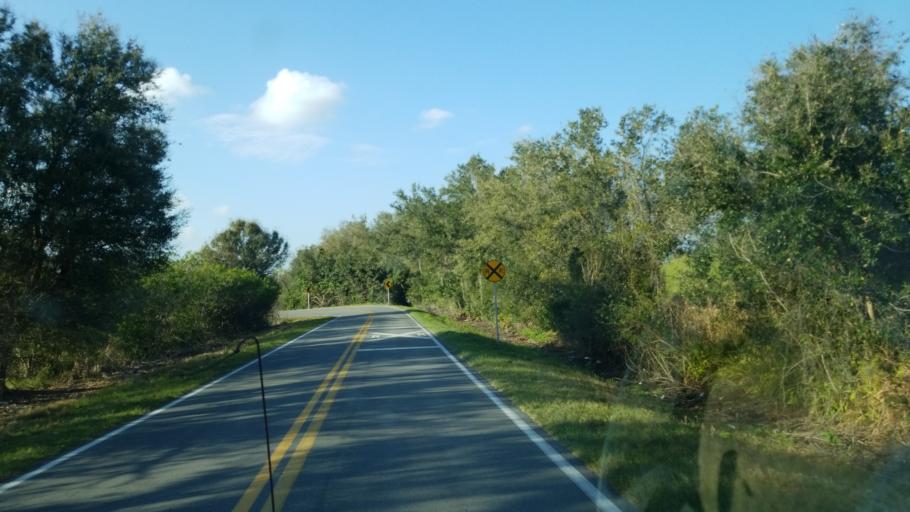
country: US
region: Florida
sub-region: Polk County
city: Mulberry
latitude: 27.7727
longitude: -81.9740
